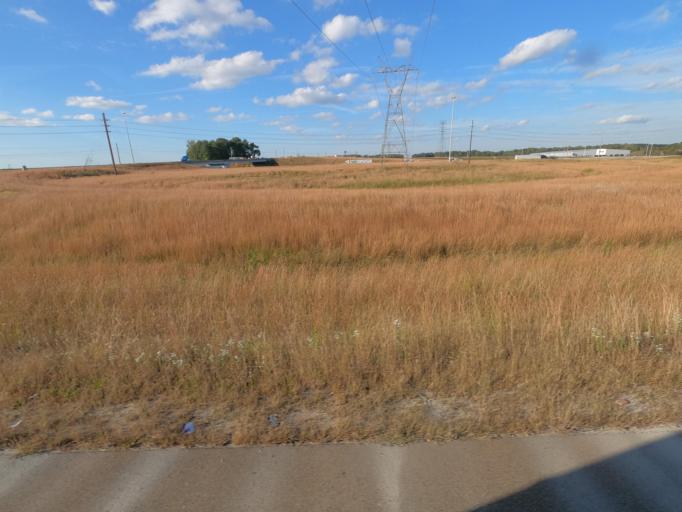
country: US
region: Tennessee
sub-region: Madison County
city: Jackson
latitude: 35.6772
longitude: -88.7790
